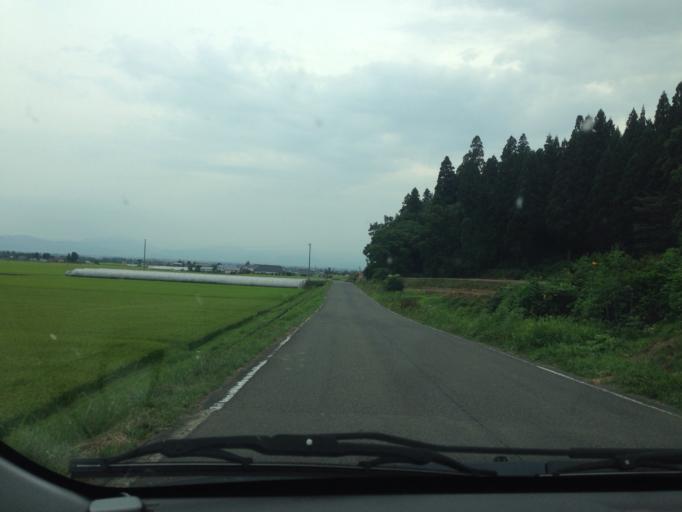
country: JP
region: Fukushima
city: Kitakata
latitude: 37.6553
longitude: 139.8460
